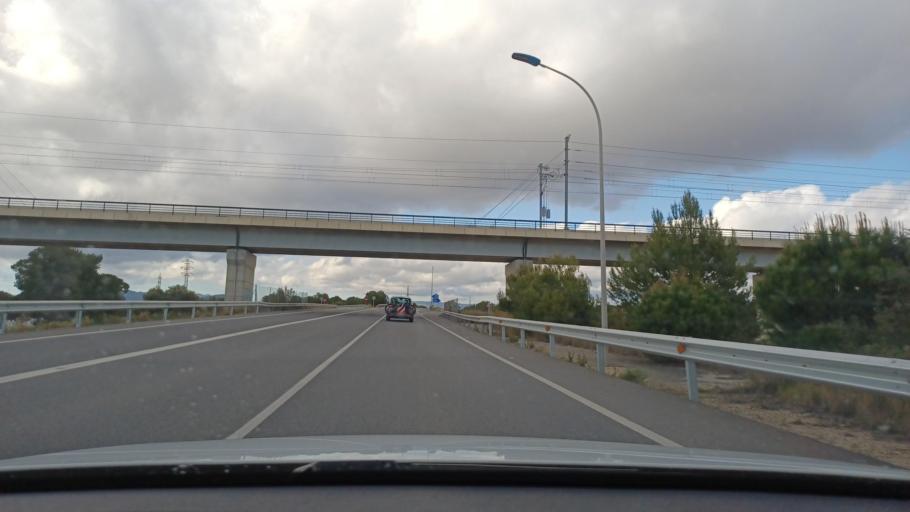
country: ES
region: Catalonia
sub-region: Provincia de Tarragona
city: Cambrils
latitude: 41.0793
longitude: 1.0418
